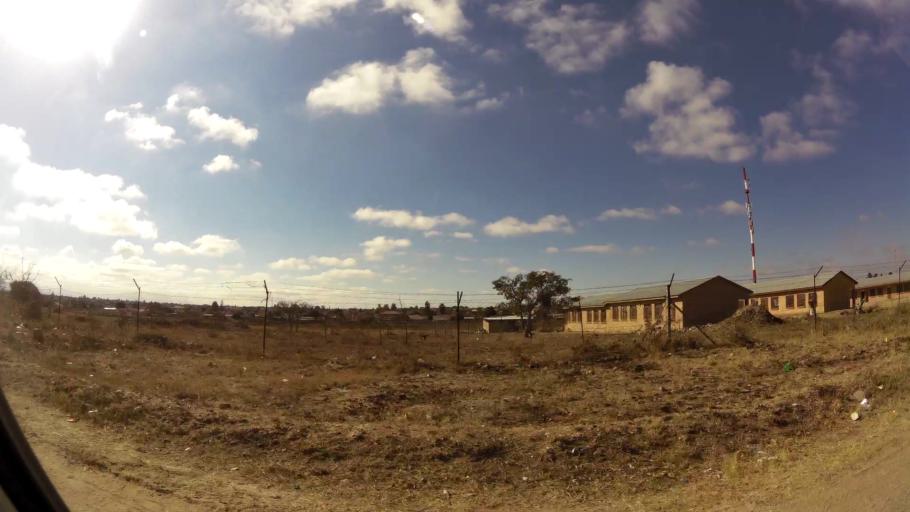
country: ZA
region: Limpopo
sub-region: Capricorn District Municipality
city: Polokwane
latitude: -23.8566
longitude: 29.3667
